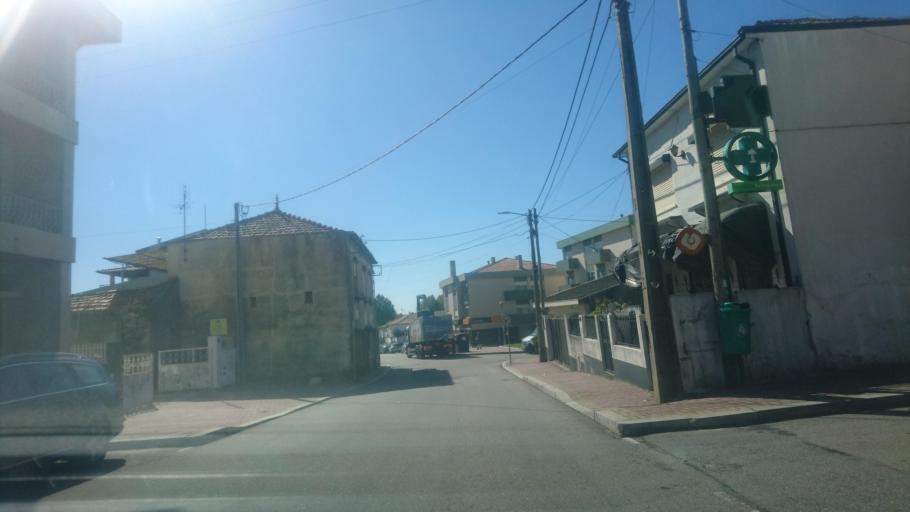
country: PT
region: Aveiro
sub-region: Santa Maria da Feira
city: Lamas
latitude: 40.9809
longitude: -8.5708
